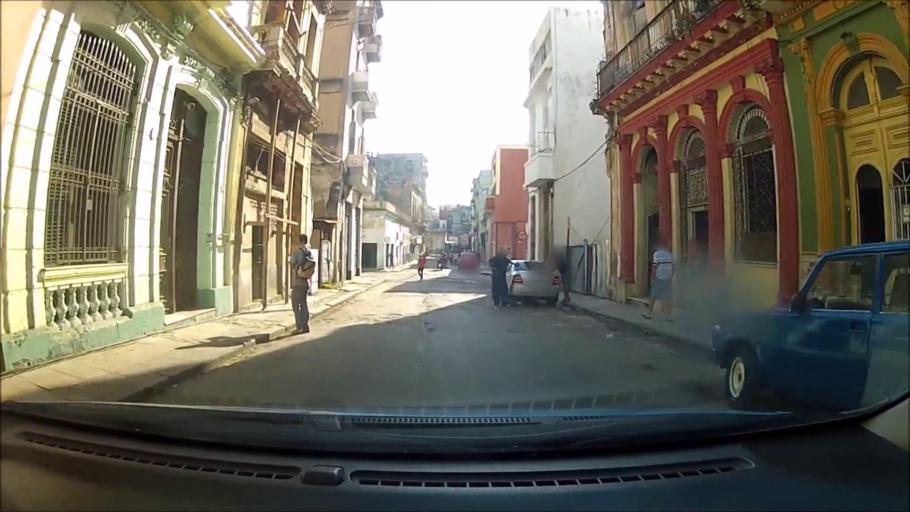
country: CU
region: La Habana
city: Centro Habana
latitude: 23.1386
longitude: -82.3627
